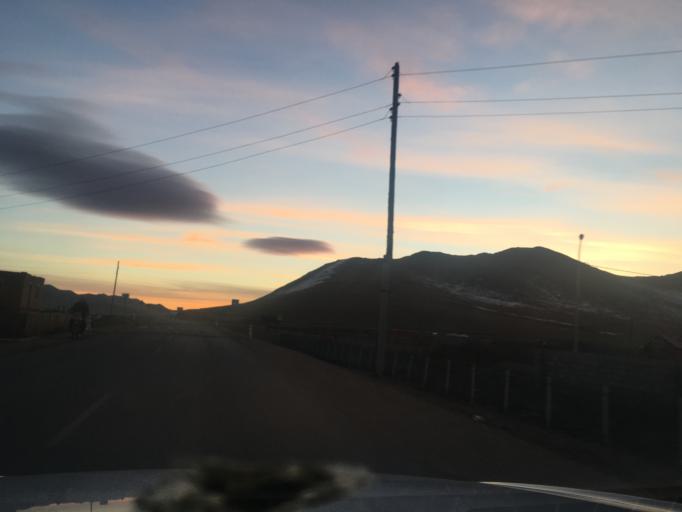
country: MN
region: Central Aimak
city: Mandal
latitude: 48.1211
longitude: 106.6494
